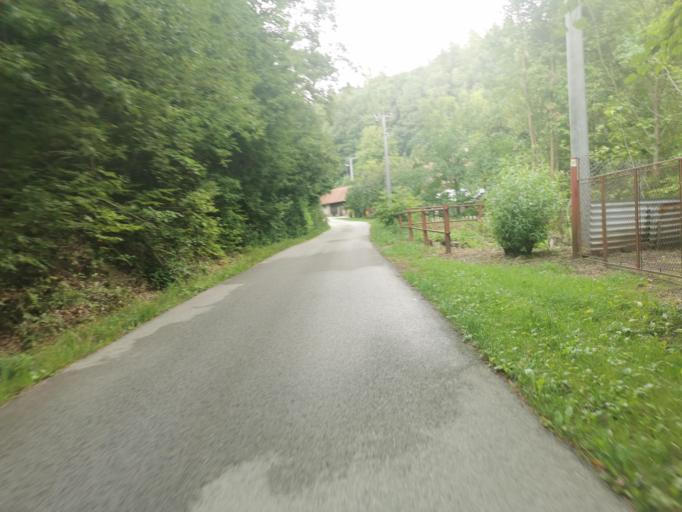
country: SK
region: Trenciansky
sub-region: Okres Myjava
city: Myjava
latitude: 48.8086
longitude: 17.5659
